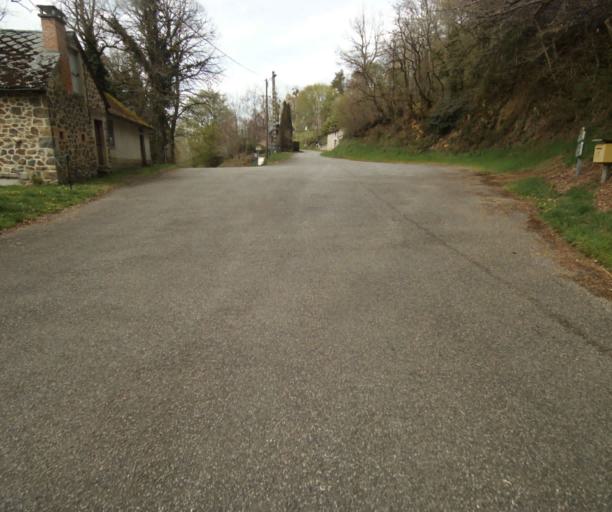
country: FR
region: Limousin
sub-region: Departement de la Correze
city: Laguenne
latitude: 45.2259
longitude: 1.8594
